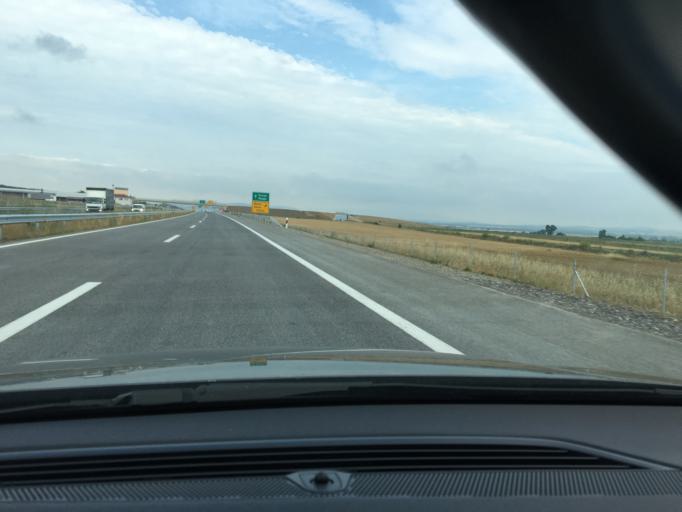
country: MK
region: Sveti Nikole
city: Sveti Nikole
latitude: 41.8100
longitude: 22.0529
